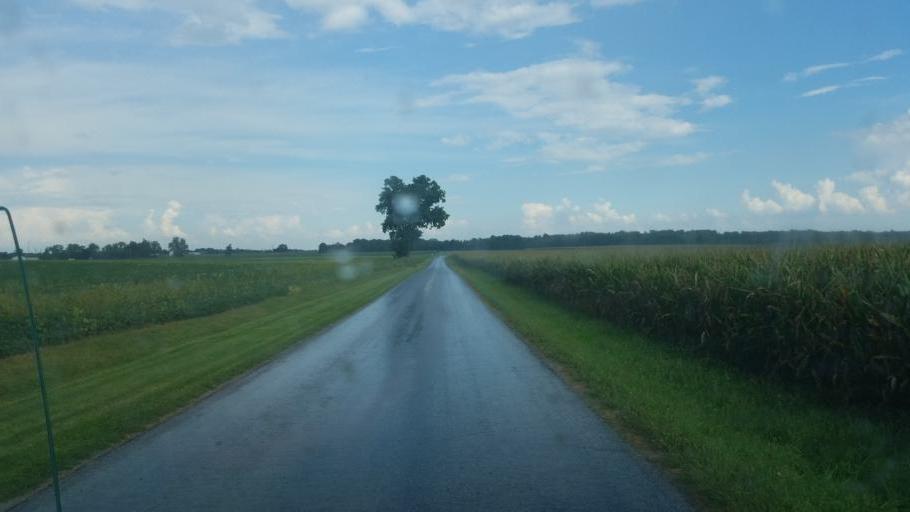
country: US
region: Ohio
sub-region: Huron County
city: Greenwich
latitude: 41.0095
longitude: -82.5647
